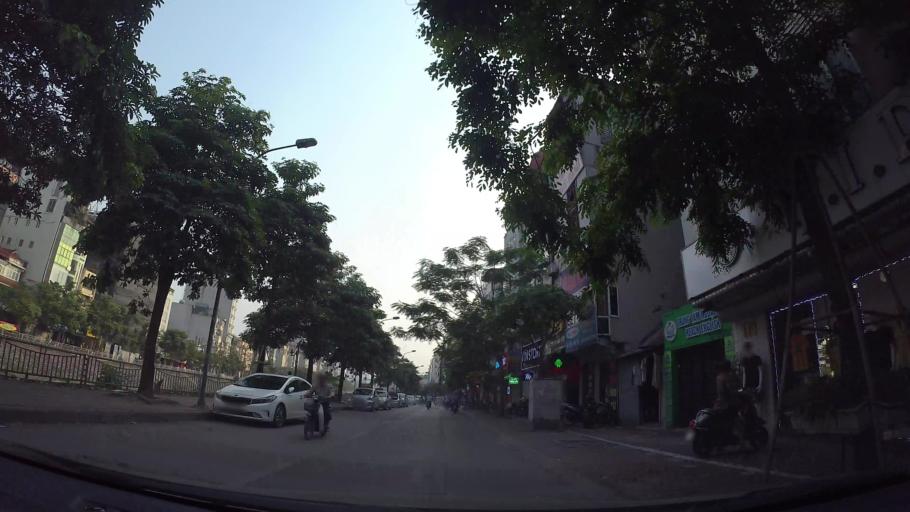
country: VN
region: Ha Noi
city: Thanh Xuan
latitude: 20.9987
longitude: 105.8171
